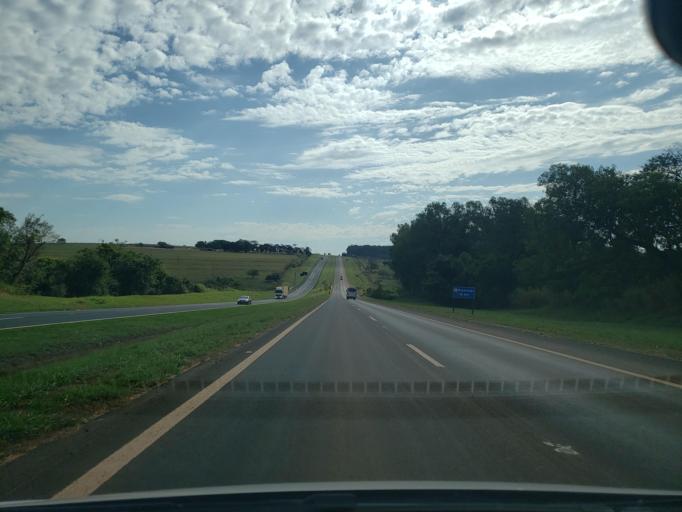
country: BR
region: Sao Paulo
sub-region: Promissao
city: Promissao
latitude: -21.6113
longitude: -49.8684
